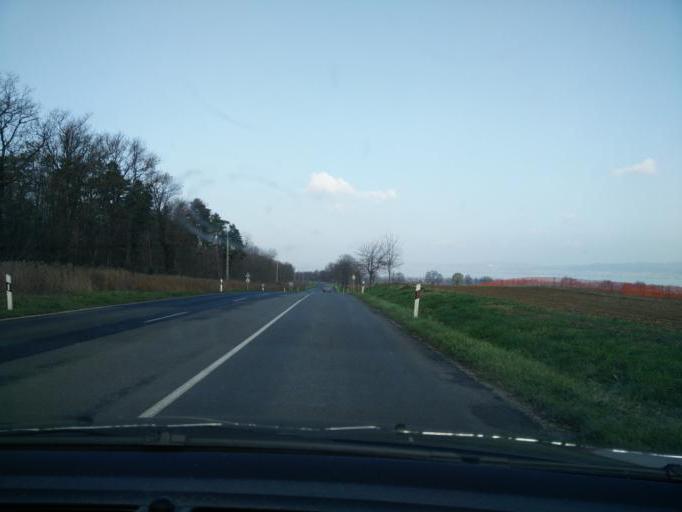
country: HU
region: Somogy
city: Balatonbereny
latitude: 46.6885
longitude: 17.3289
